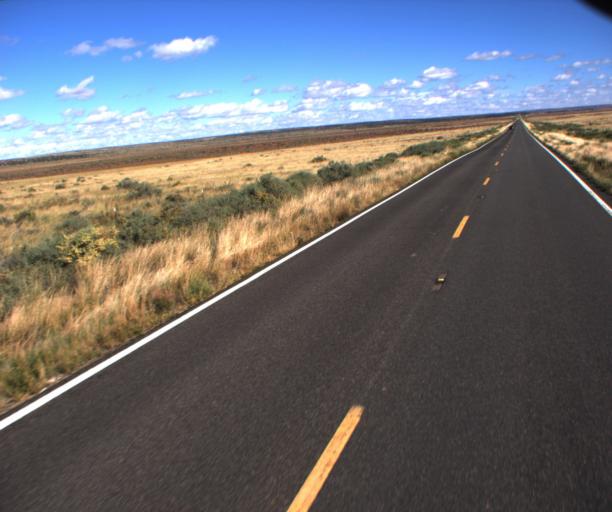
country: US
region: Arizona
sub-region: Apache County
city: Saint Johns
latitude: 34.6828
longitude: -109.2811
